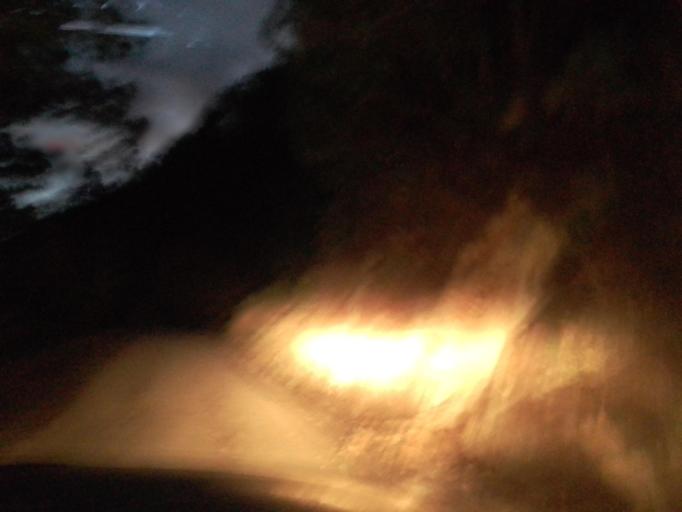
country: GT
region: San Marcos
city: Tacana
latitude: 15.2362
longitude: -92.1988
